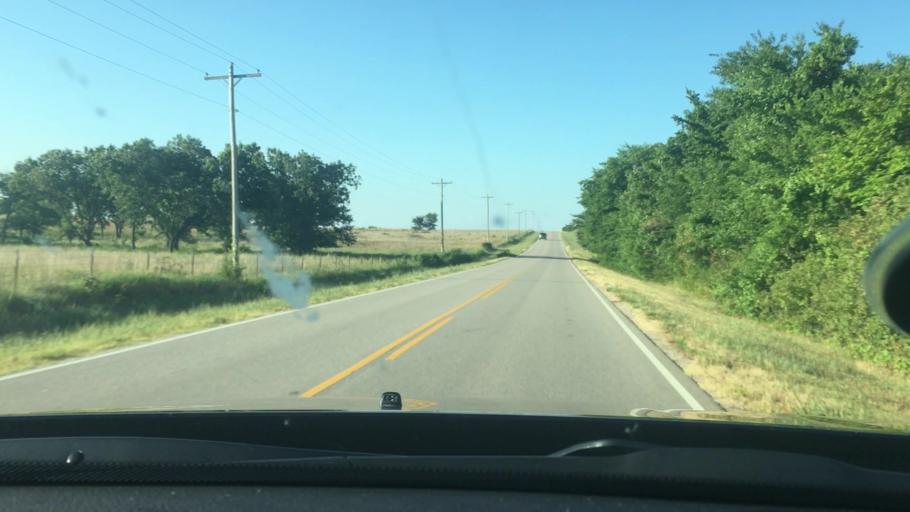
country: US
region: Oklahoma
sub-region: Murray County
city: Sulphur
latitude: 34.6005
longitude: -96.8449
